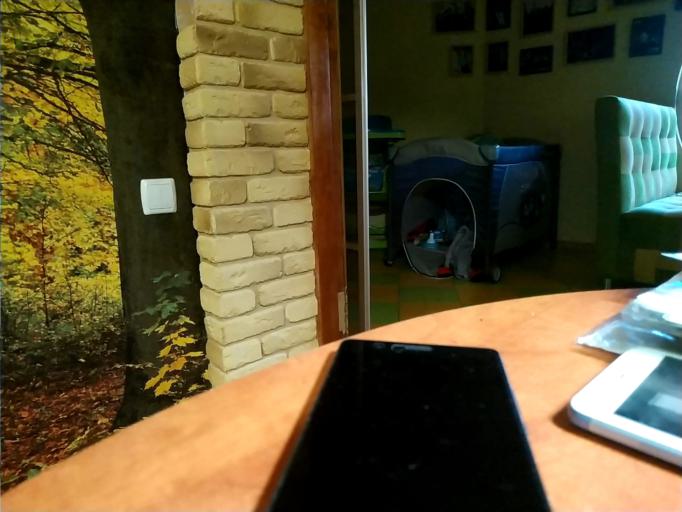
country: RU
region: Orjol
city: Znamenskoye
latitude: 53.4940
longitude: 35.5096
